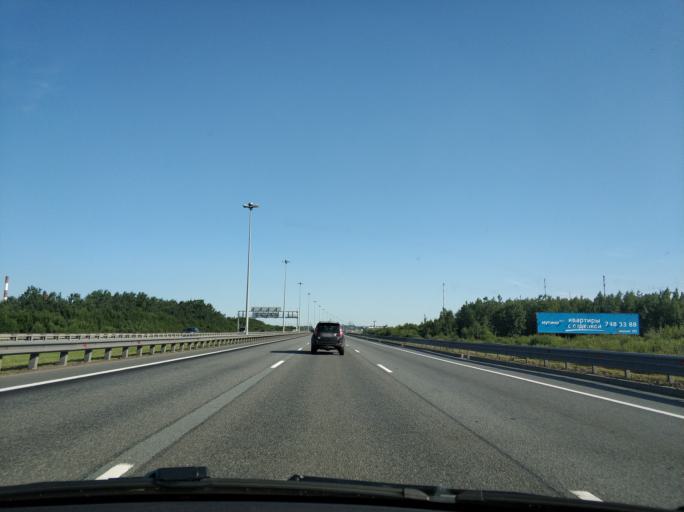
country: RU
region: Leningrad
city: Bugry
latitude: 60.0689
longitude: 30.3839
